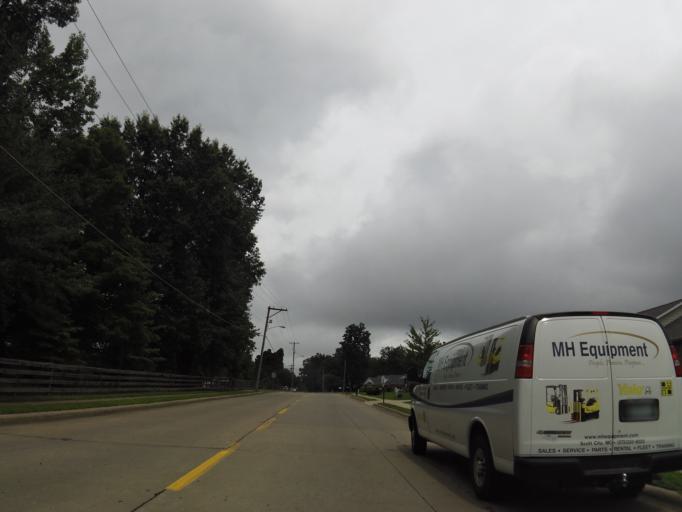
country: US
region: Missouri
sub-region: Cape Girardeau County
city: Cape Girardeau
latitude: 37.3418
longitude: -89.5555
